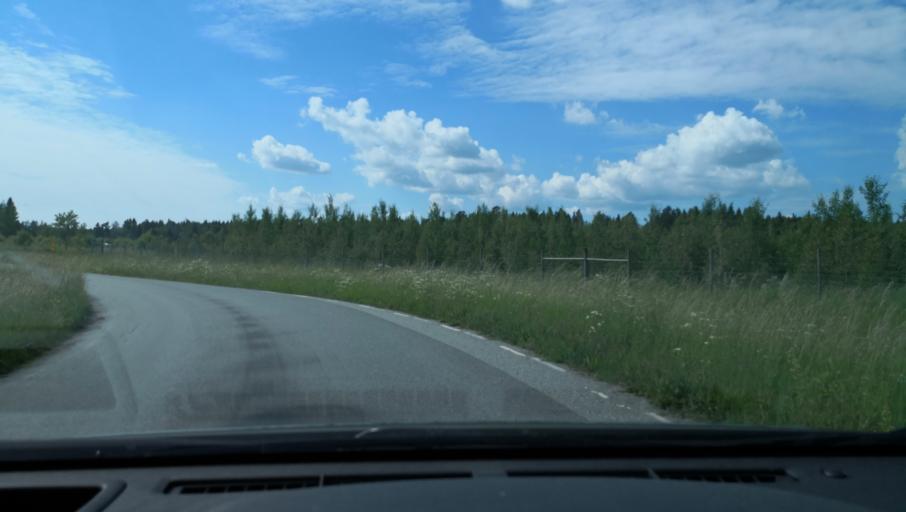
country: SE
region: Uppsala
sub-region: Enkopings Kommun
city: Orsundsbro
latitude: 59.8161
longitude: 17.3681
